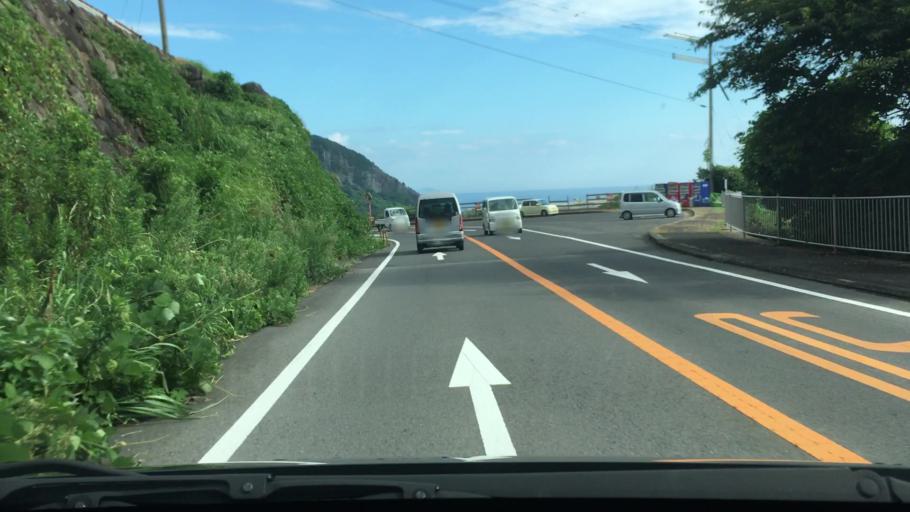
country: JP
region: Nagasaki
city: Togitsu
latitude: 32.8430
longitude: 129.6991
